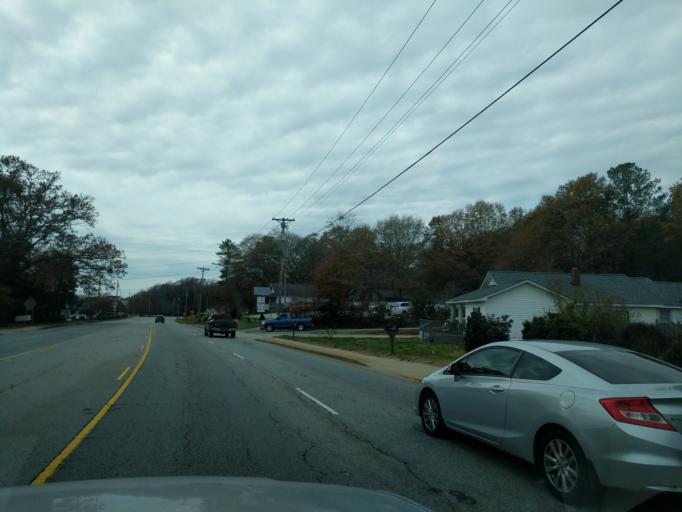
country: US
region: South Carolina
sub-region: Pickens County
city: Easley
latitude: 34.8367
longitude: -82.6206
